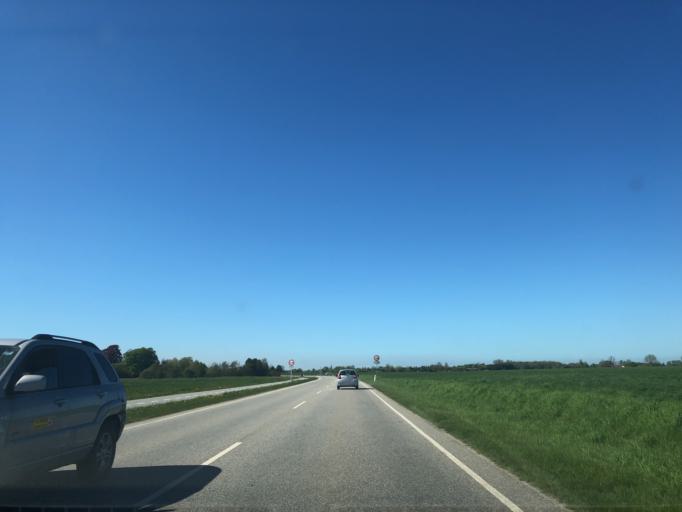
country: DK
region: Zealand
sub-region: Stevns Kommune
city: Store Heddinge
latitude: 55.3471
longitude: 12.3356
